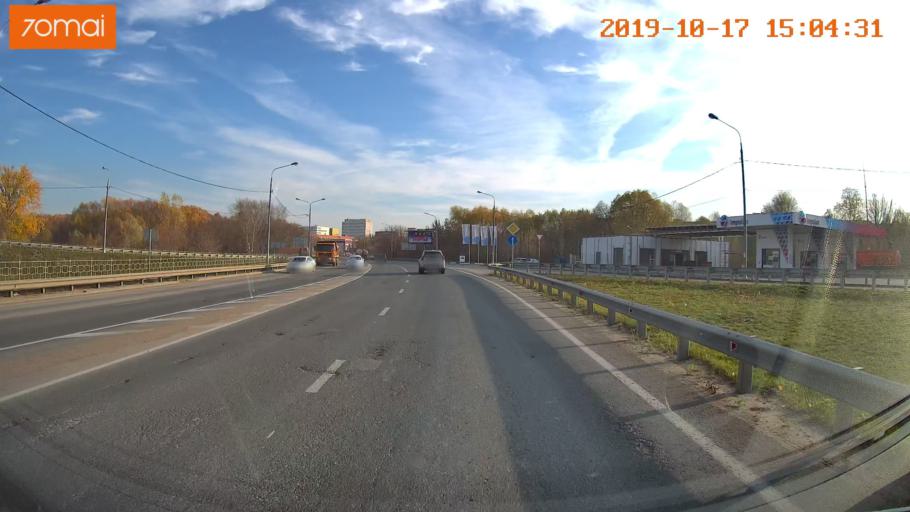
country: RU
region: Rjazan
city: Ryazan'
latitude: 54.6394
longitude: 39.7199
